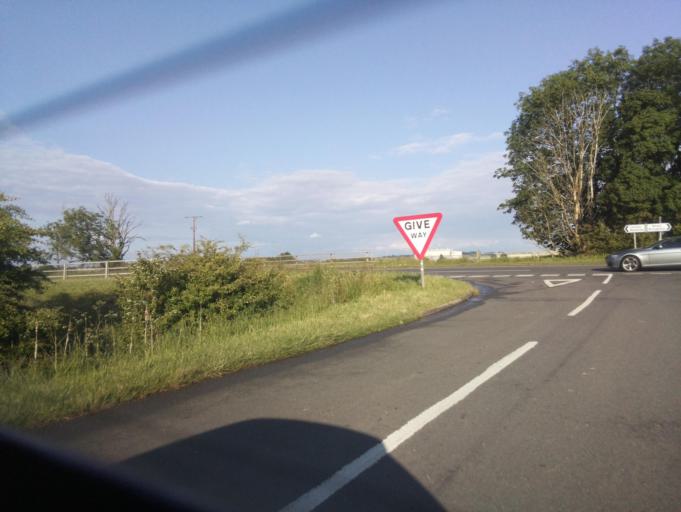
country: GB
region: England
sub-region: Lincolnshire
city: Navenby
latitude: 53.1126
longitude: -0.5987
